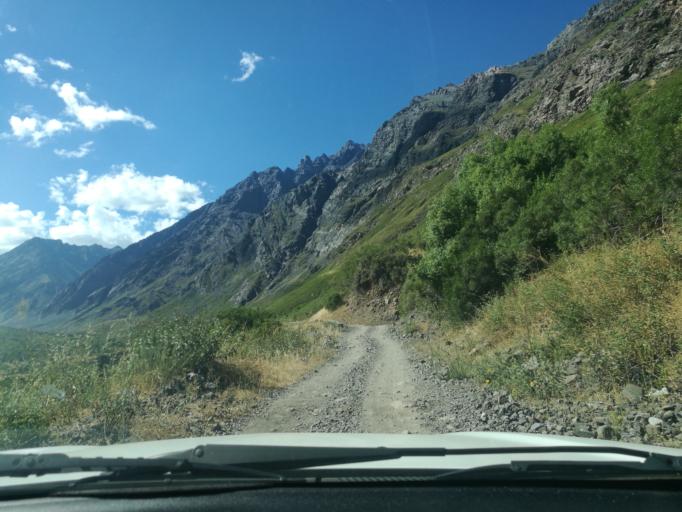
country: CL
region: O'Higgins
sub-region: Provincia de Cachapoal
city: Machali
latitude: -34.3854
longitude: -70.2822
